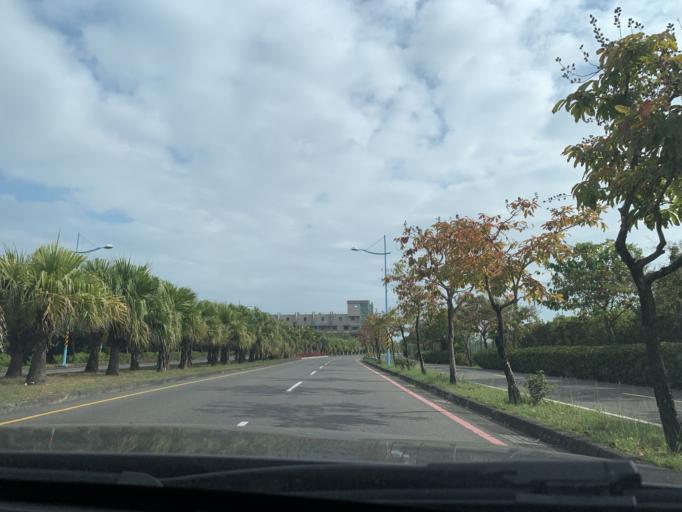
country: TW
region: Taiwan
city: Fengshan
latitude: 22.4538
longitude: 120.4865
